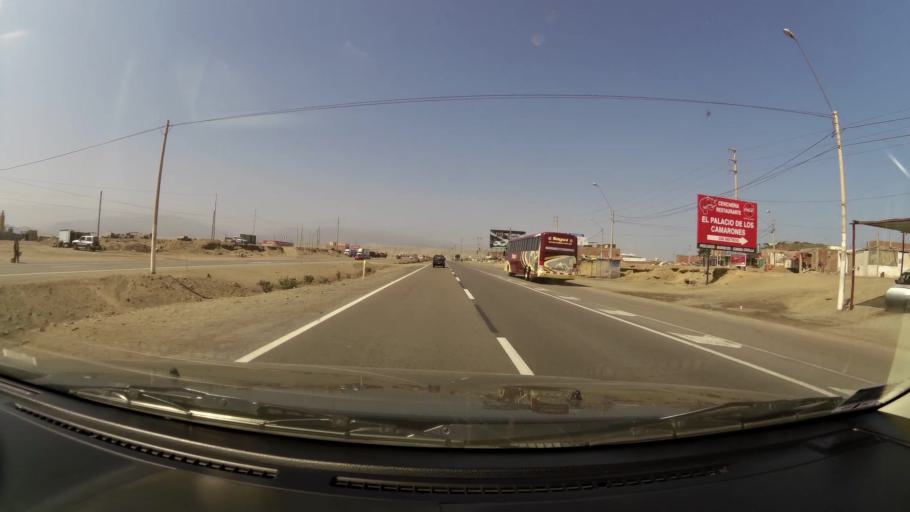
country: PE
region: Lima
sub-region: Provincia de Canete
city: Asia
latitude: -12.7890
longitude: -76.5675
